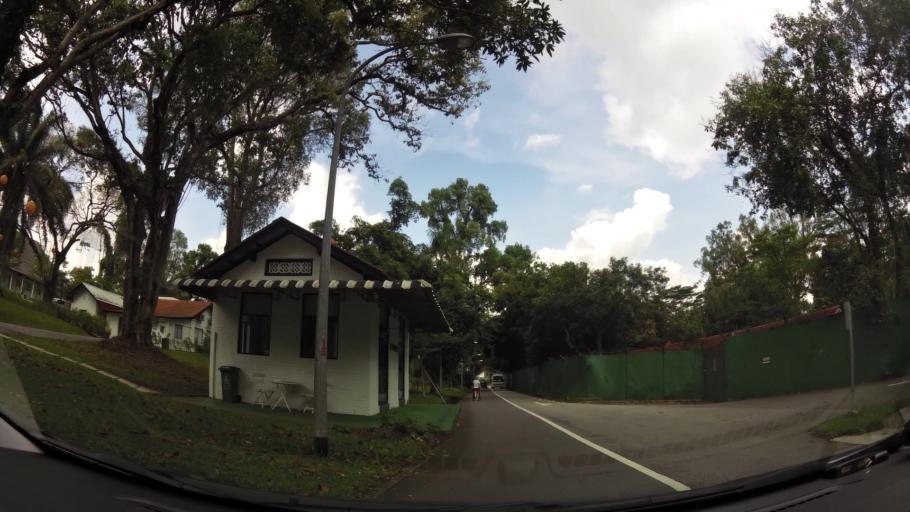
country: SG
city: Singapore
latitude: 1.3023
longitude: 103.8122
